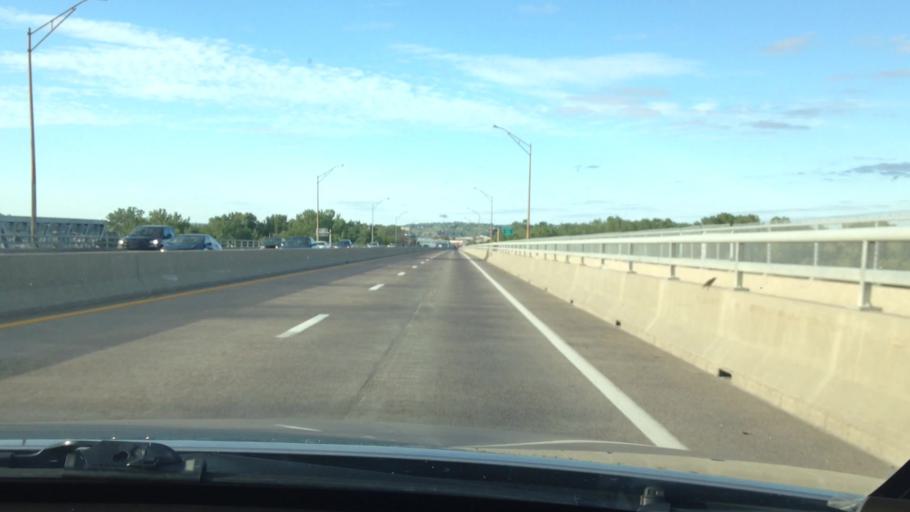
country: US
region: Missouri
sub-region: Jackson County
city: Kansas City
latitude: 39.1161
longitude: -94.5786
